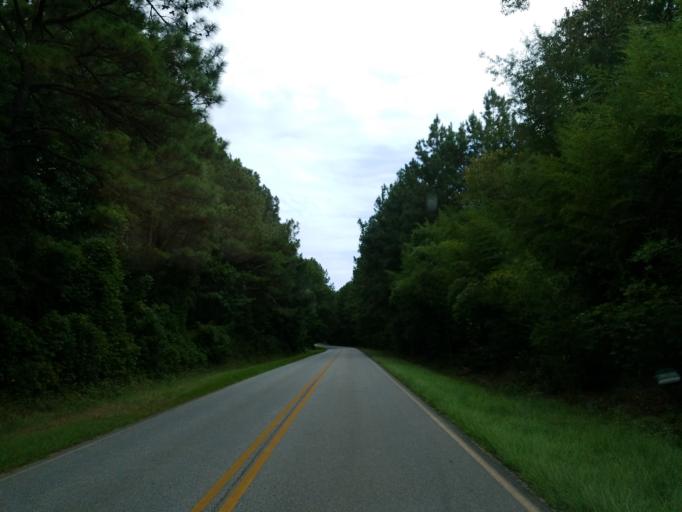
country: US
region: Georgia
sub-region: Monroe County
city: Forsyth
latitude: 32.9142
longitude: -83.9122
